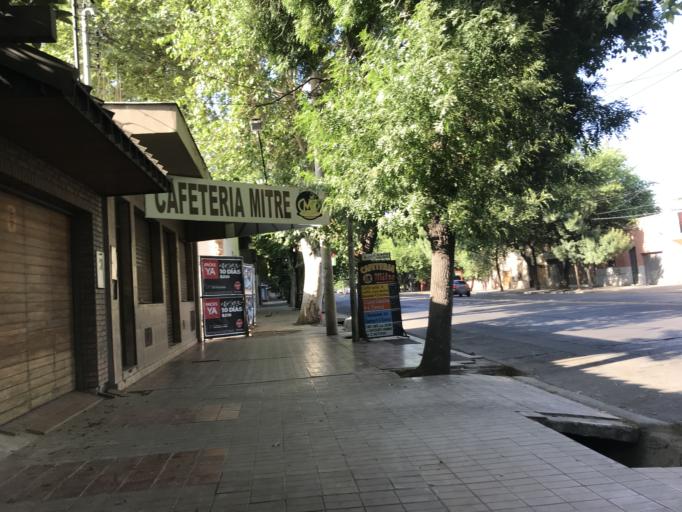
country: AR
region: Mendoza
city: Mendoza
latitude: -32.8798
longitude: -68.8418
